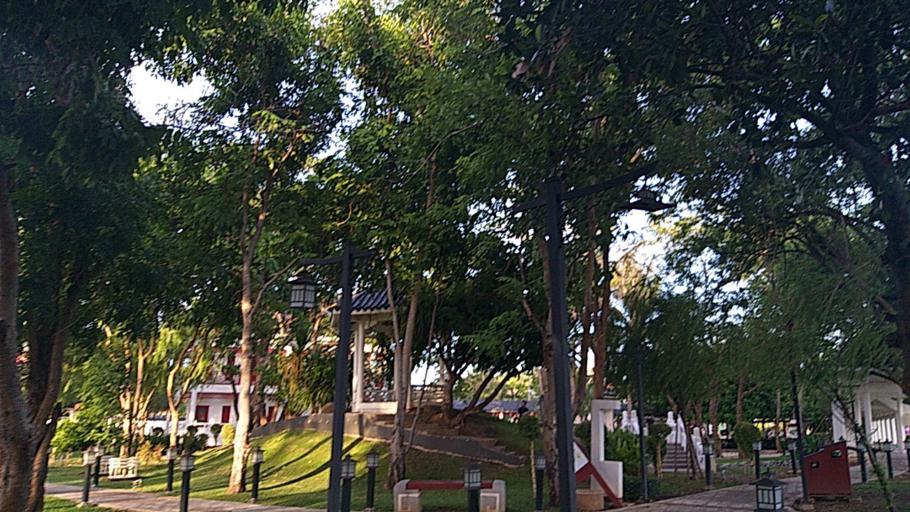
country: TH
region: Khon Kaen
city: Khon Kaen
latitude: 16.4187
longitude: 102.8393
